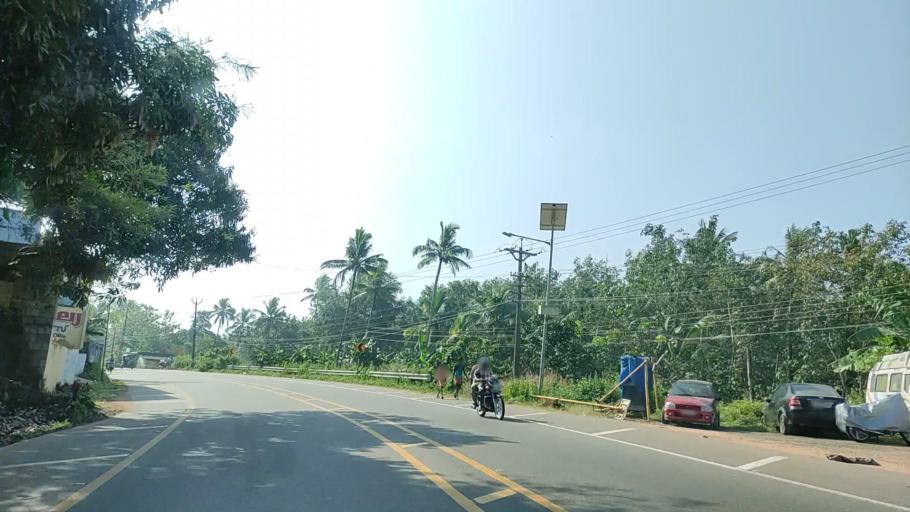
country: IN
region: Kerala
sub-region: Kollam
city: Punalur
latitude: 8.8781
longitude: 76.8667
